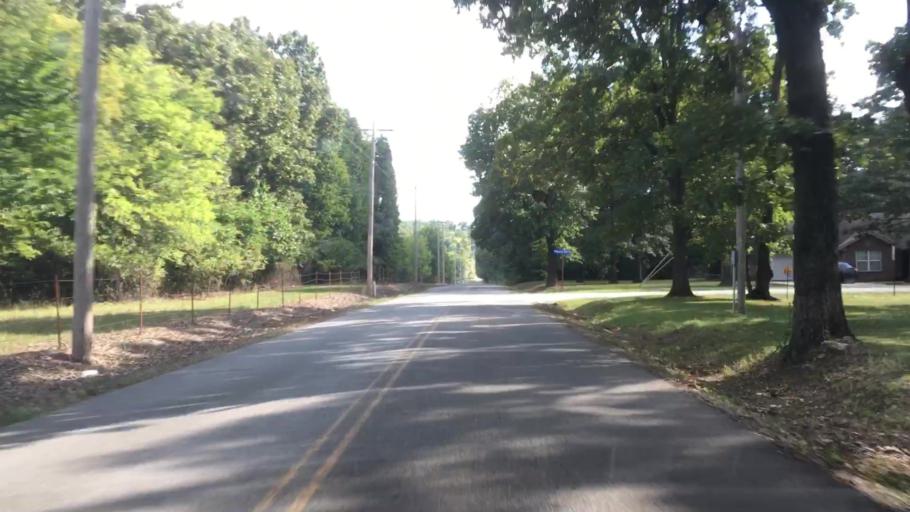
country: US
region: Oklahoma
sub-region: Cherokee County
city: Park Hill
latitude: 35.8031
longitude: -95.0739
